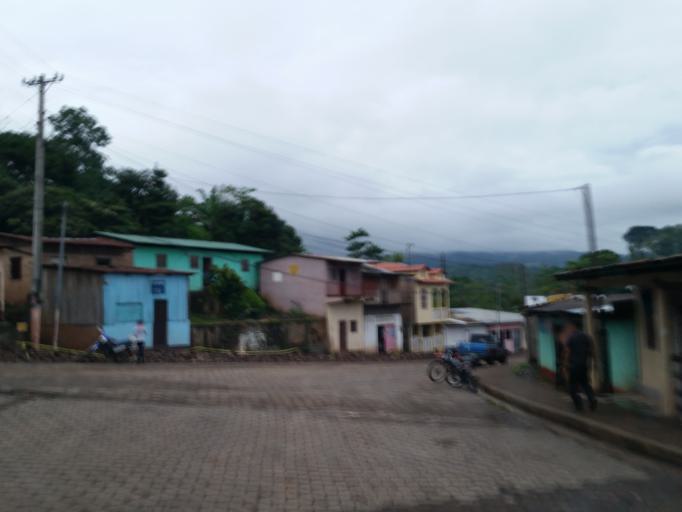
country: NI
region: Matagalpa
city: San Ramon
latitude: 13.1404
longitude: -85.7350
